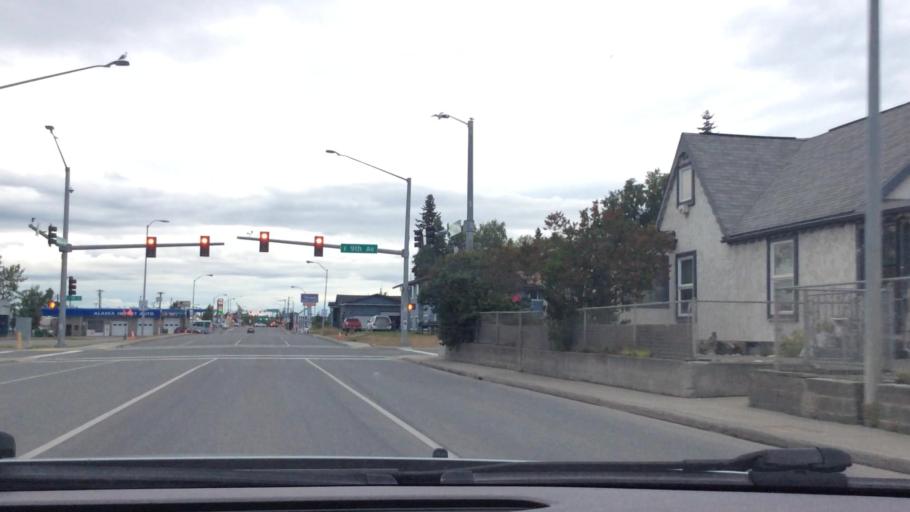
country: US
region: Alaska
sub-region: Anchorage Municipality
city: Anchorage
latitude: 61.2132
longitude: -149.8669
